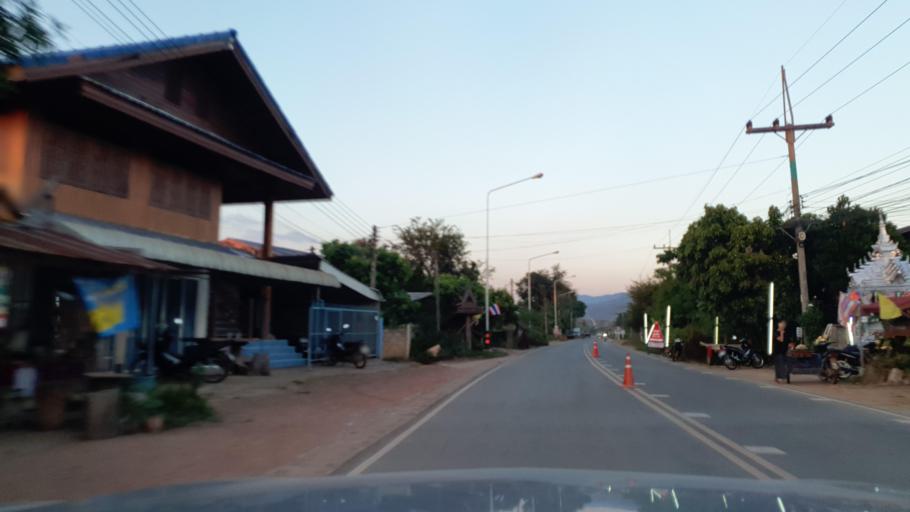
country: TH
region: Phayao
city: Dok Kham Tai
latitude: 19.0273
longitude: 100.0628
